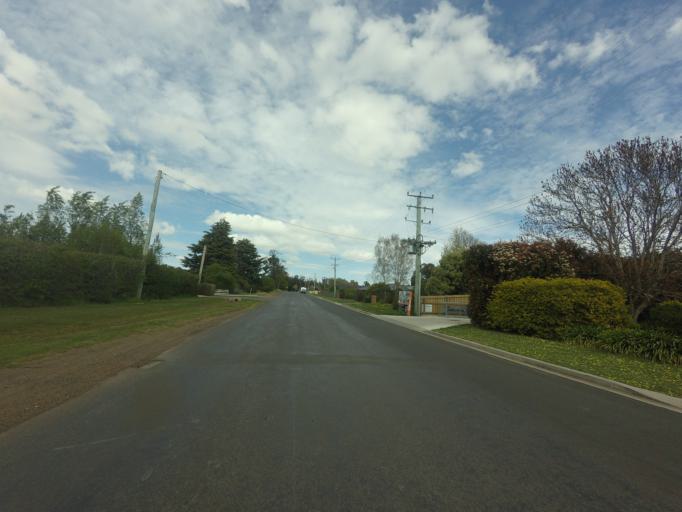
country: AU
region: Tasmania
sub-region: Northern Midlands
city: Longford
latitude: -41.6099
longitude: 147.1275
